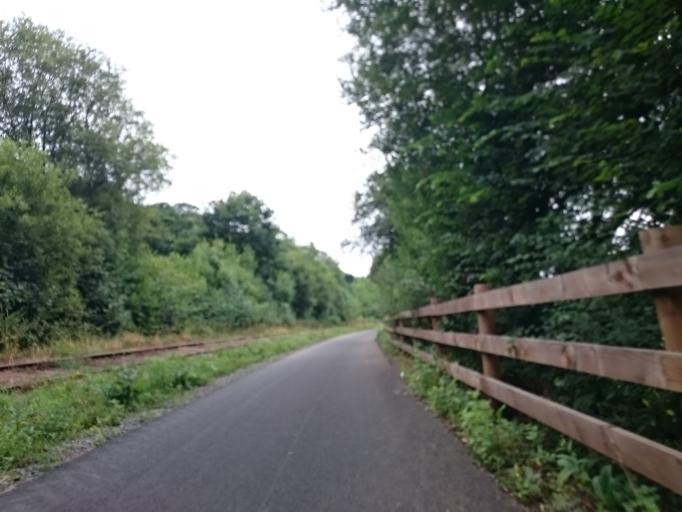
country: FR
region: Lower Normandy
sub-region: Departement du Calvados
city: Sainte-Honorine-du-Fay
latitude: 49.0485
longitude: -0.4582
